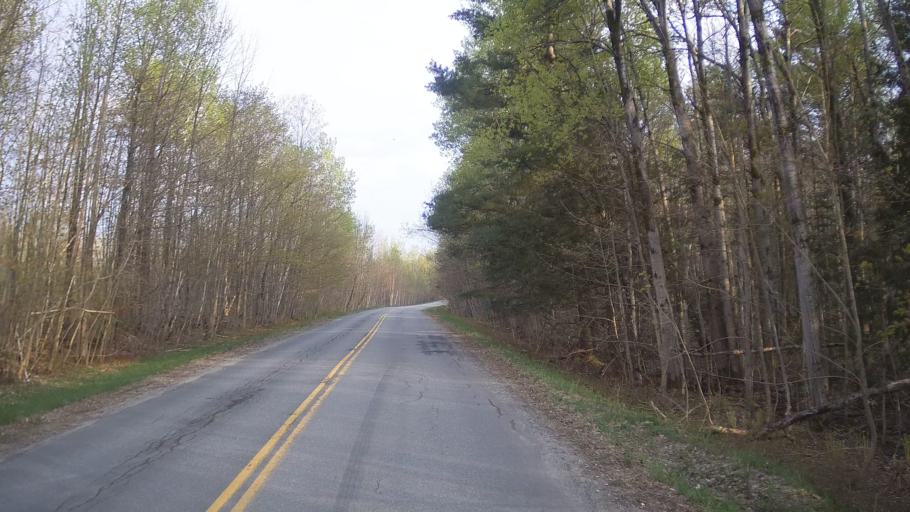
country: US
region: Vermont
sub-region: Orleans County
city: Newport
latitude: 44.9409
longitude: -72.4379
